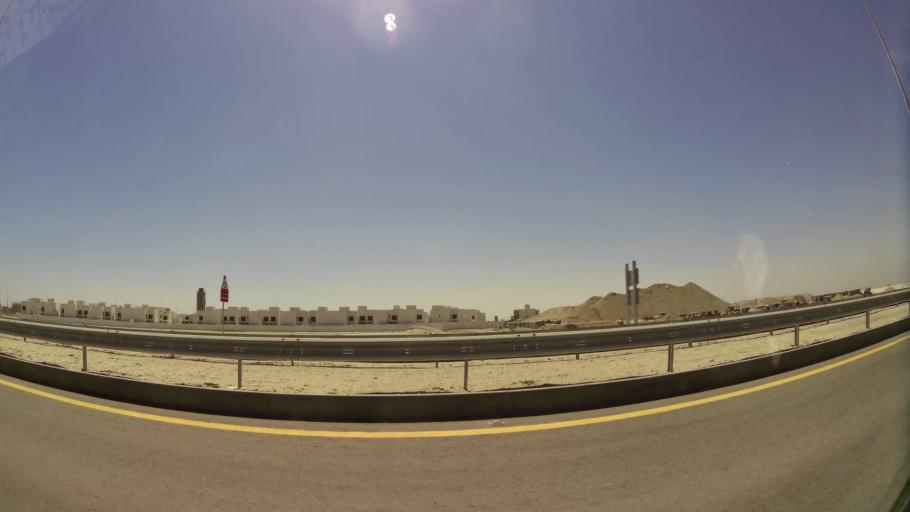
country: BH
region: Muharraq
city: Al Muharraq
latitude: 26.3038
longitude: 50.6339
